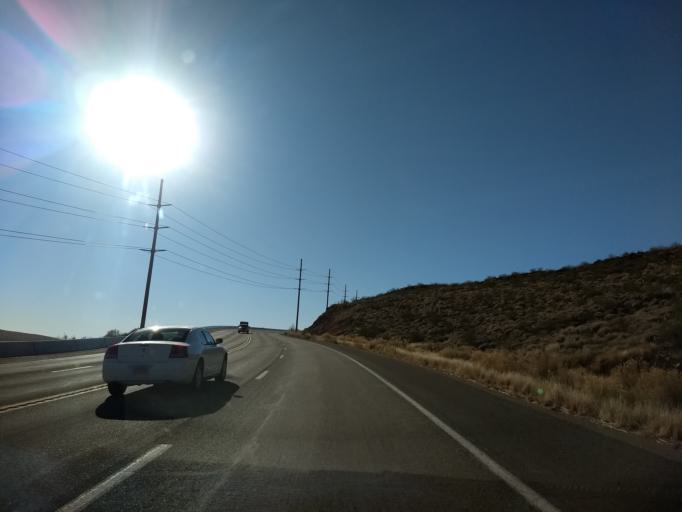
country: US
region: Utah
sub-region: Washington County
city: Washington
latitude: 37.1406
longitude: -113.4639
